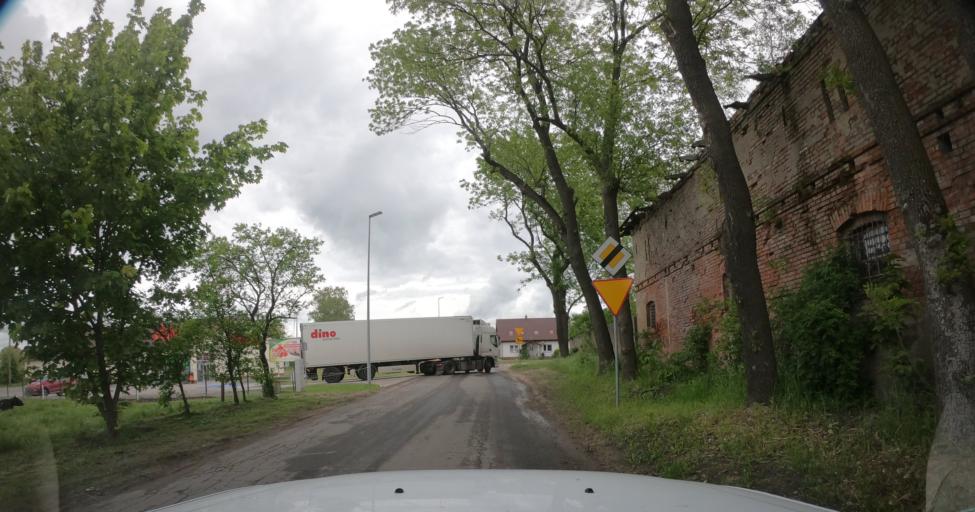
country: PL
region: West Pomeranian Voivodeship
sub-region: Powiat pyrzycki
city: Kozielice
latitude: 53.1079
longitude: 14.8151
